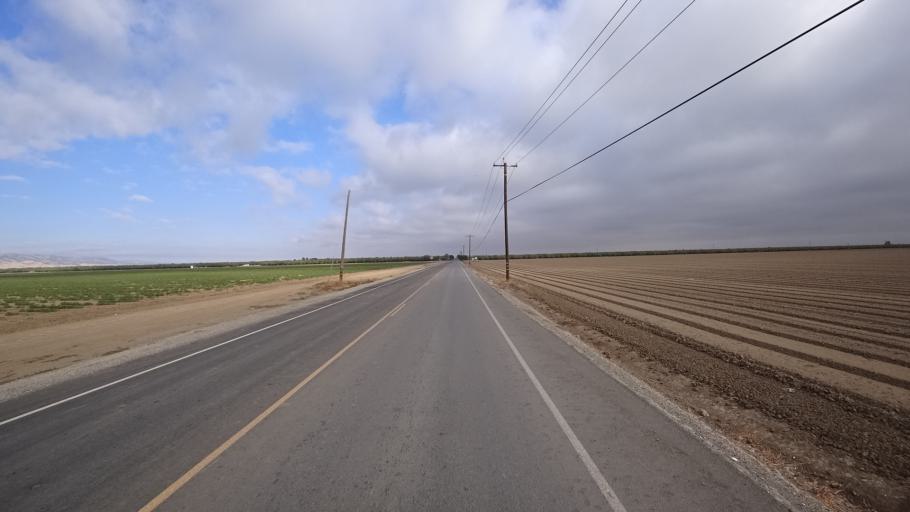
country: US
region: California
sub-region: Yolo County
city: Esparto
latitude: 38.7189
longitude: -122.0094
